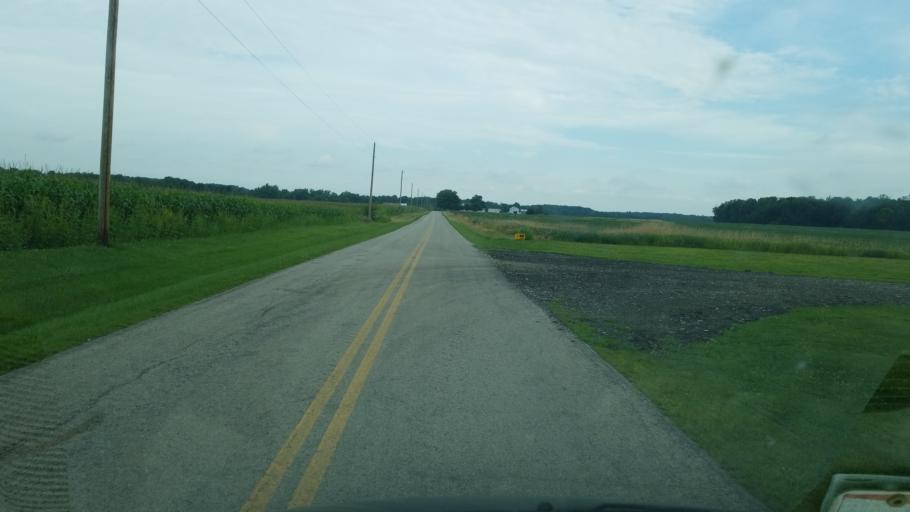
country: US
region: Ohio
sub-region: Seneca County
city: Tiffin
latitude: 41.0381
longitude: -83.0545
